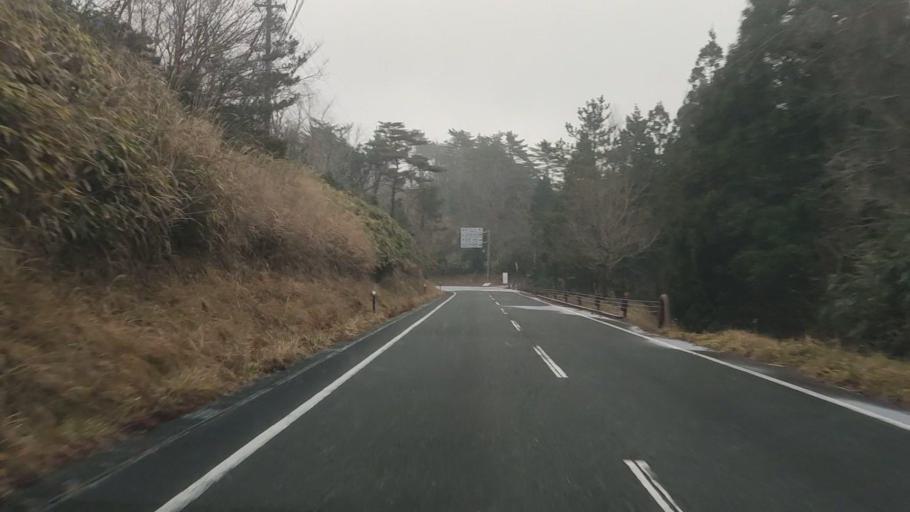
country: JP
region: Kumamoto
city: Matsubase
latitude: 32.5707
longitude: 130.9077
